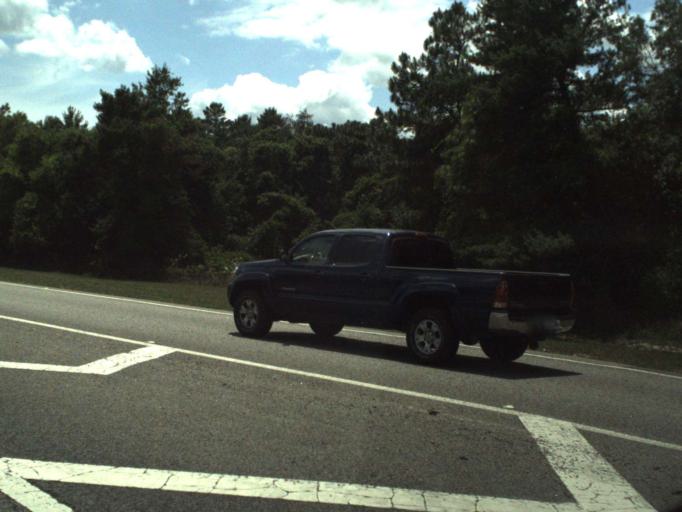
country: US
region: Florida
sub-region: Volusia County
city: Lake Helen
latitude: 28.9535
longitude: -81.2584
